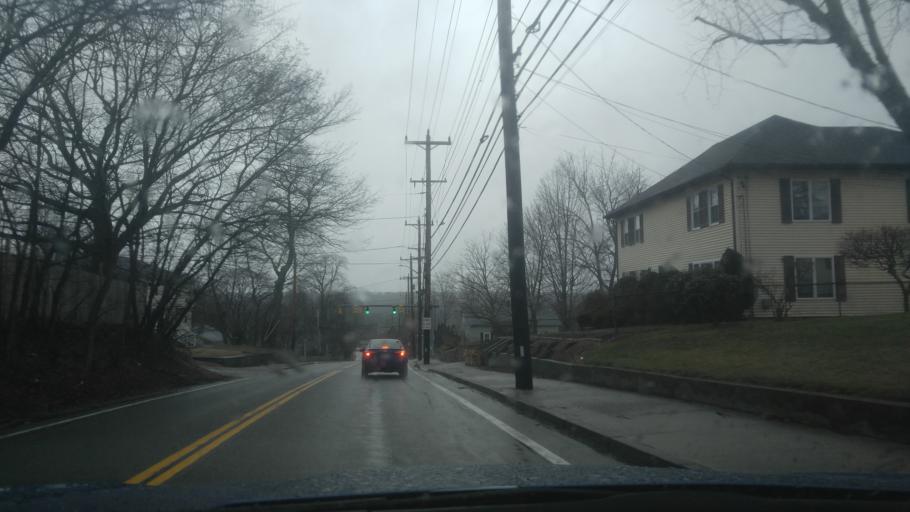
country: US
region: Rhode Island
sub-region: Kent County
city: West Warwick
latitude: 41.6846
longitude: -71.5192
